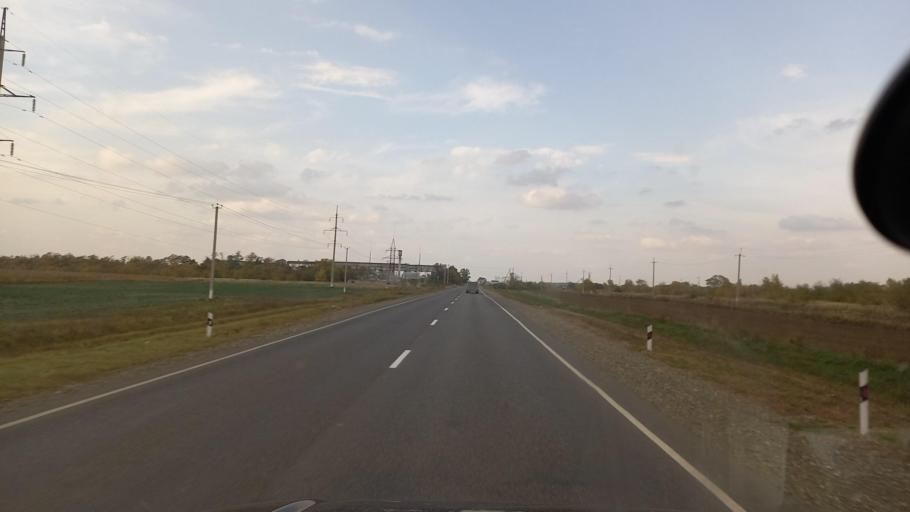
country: RU
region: Krasnodarskiy
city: Mostovskoy
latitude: 44.3711
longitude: 40.8272
